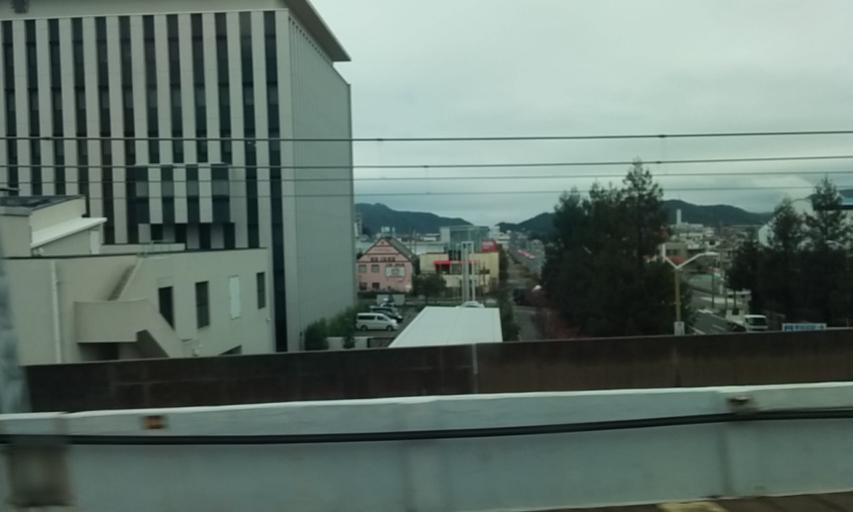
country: JP
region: Hyogo
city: Himeji
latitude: 34.8246
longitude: 134.7056
